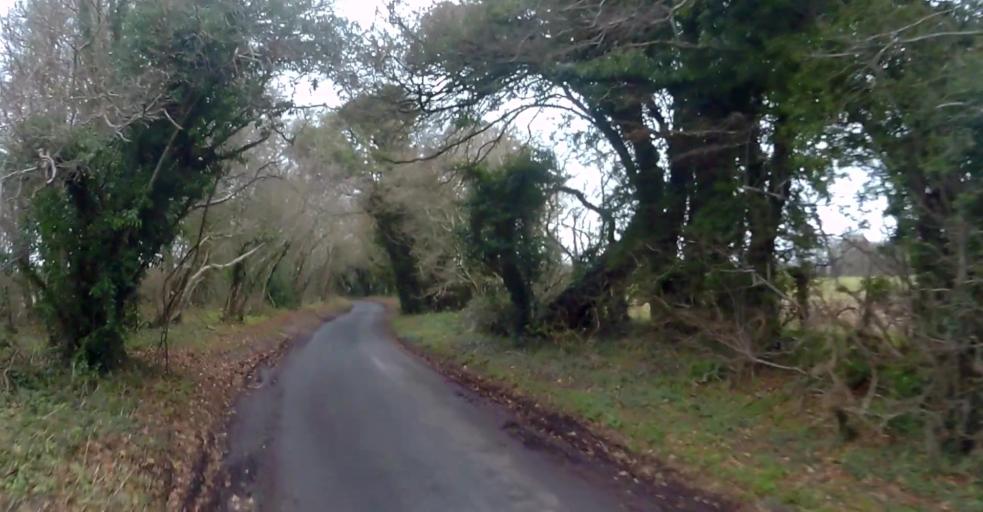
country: GB
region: England
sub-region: Hampshire
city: Overton
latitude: 51.2165
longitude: -1.2148
